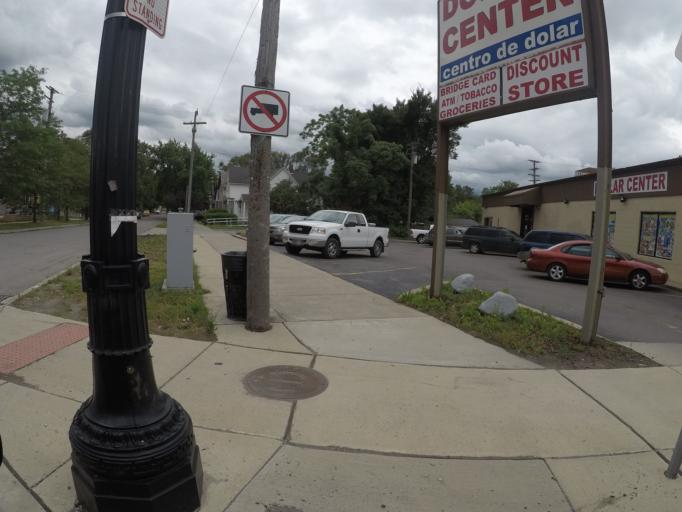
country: US
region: Michigan
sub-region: Wayne County
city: River Rouge
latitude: 42.3155
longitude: -83.1115
